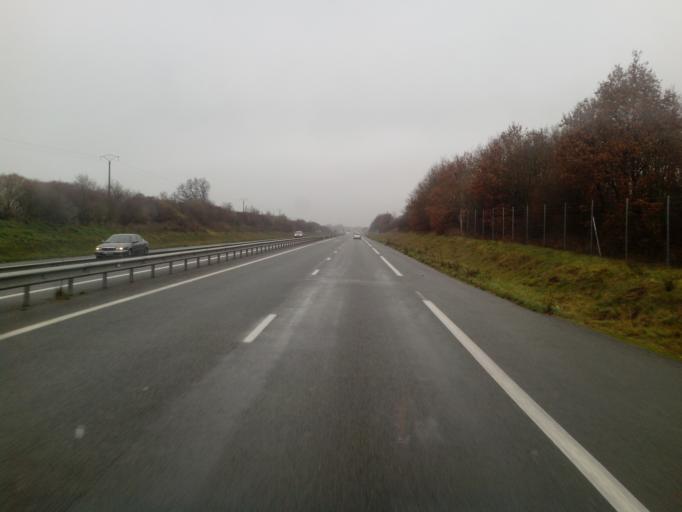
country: FR
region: Poitou-Charentes
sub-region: Departement de la Vienne
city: Savigny-Levescault
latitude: 46.5008
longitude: 0.4838
